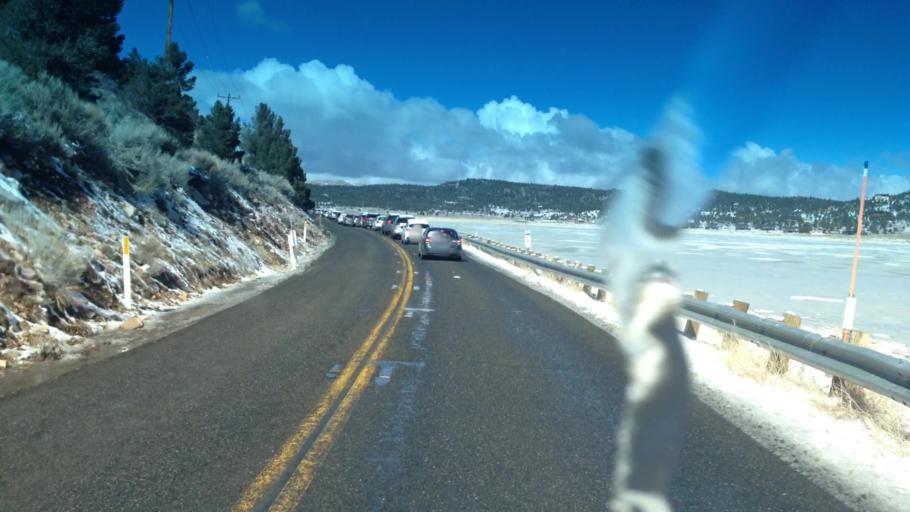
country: US
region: California
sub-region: San Bernardino County
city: Big Bear City
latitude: 34.2776
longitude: -116.8141
